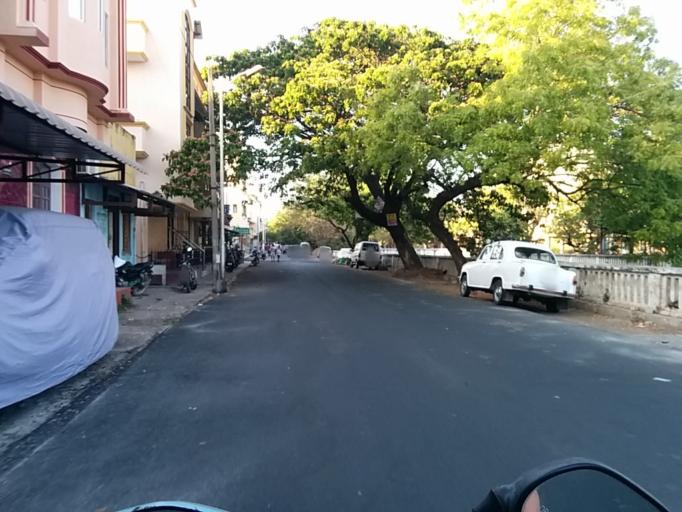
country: IN
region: Pondicherry
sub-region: Puducherry
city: Puducherry
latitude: 11.9258
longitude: 79.8309
